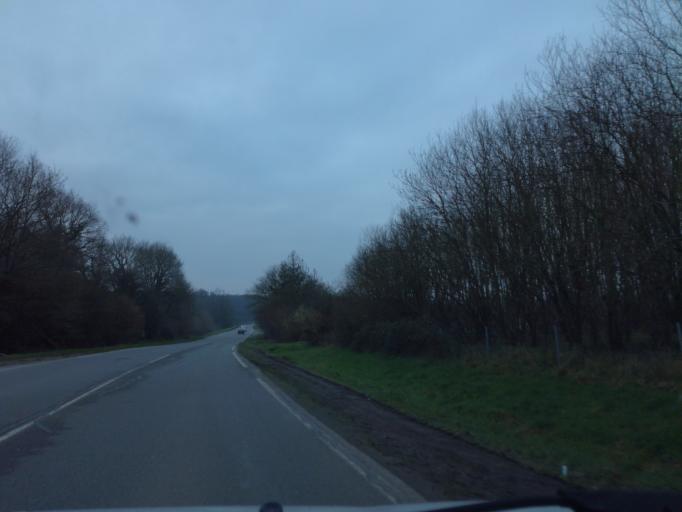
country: FR
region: Brittany
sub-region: Departement d'Ille-et-Vilaine
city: Gosne
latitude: 48.2399
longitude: -1.4617
